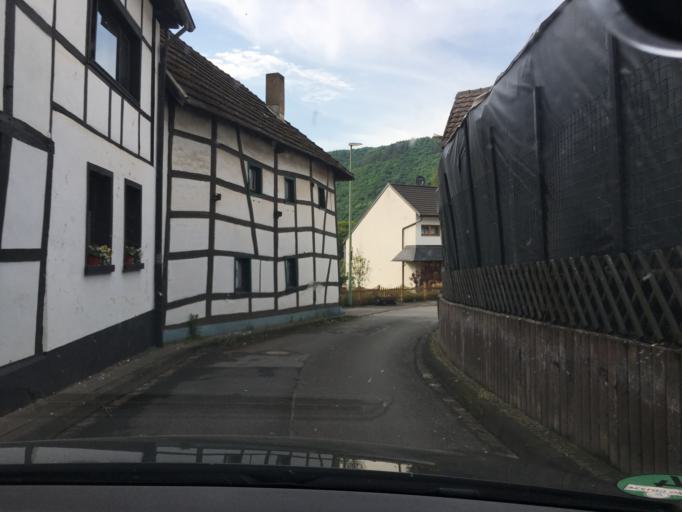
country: DE
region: North Rhine-Westphalia
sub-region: Regierungsbezirk Koln
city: Nideggen
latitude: 50.6695
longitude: 6.4783
